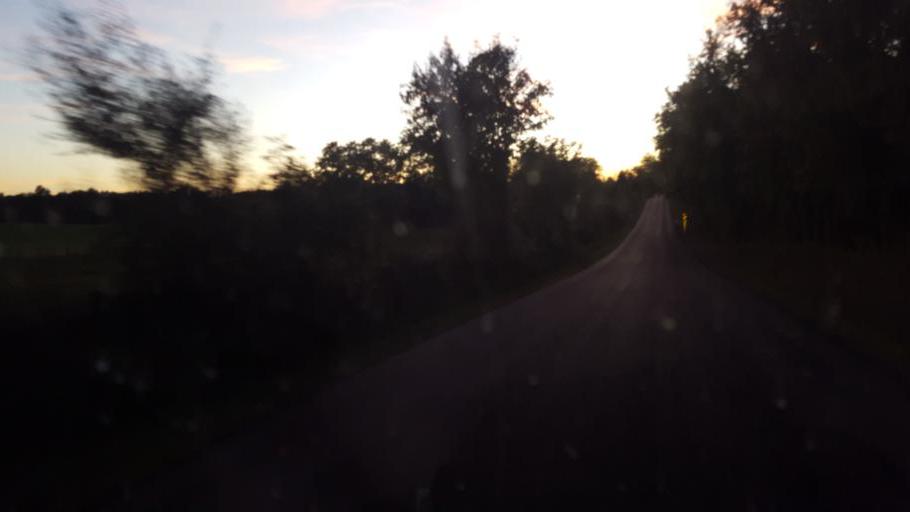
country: US
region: Ohio
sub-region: Richland County
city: Lexington
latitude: 40.6013
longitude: -82.6575
